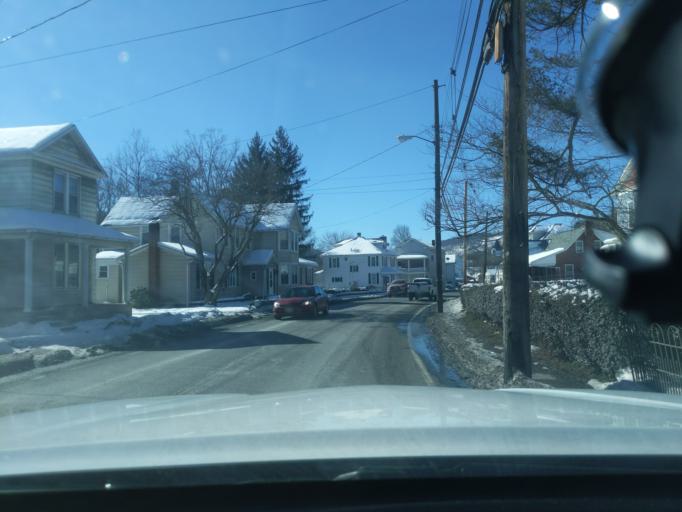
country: US
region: Maryland
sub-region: Allegany County
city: Lonaconing
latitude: 39.5708
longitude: -78.9758
